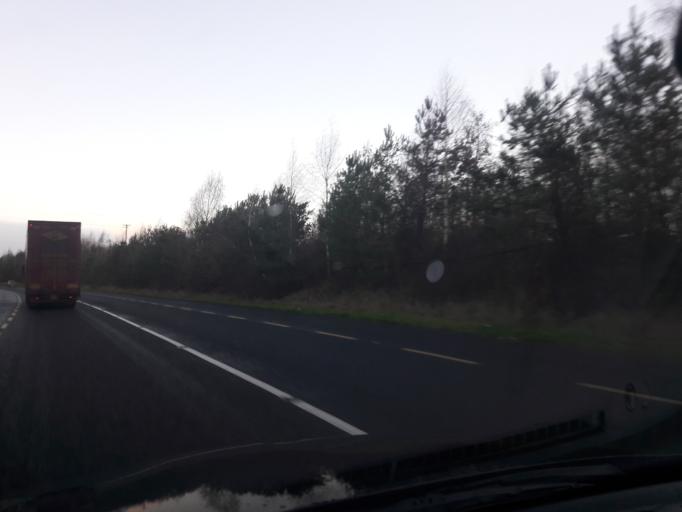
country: IE
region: Ulster
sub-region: County Monaghan
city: Monaghan
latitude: 54.2565
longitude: -6.9515
